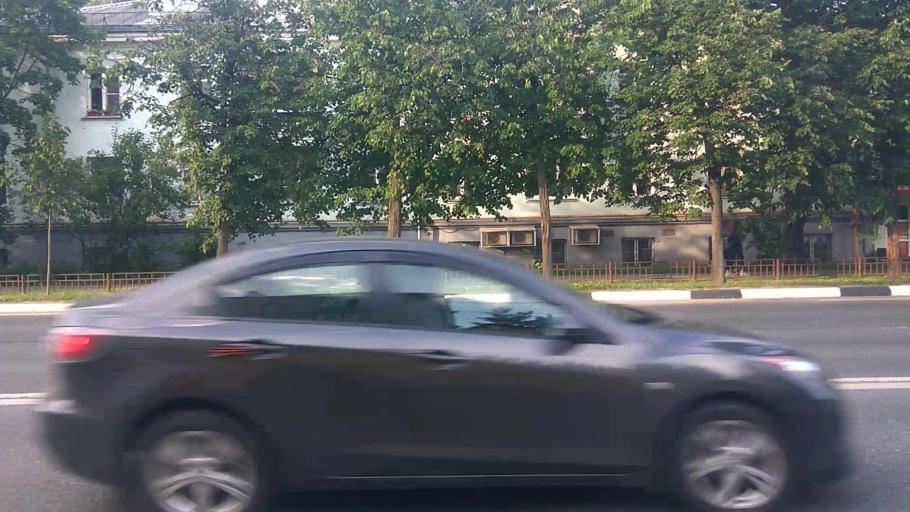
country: RU
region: Moskovskaya
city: Mytishchi
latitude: 55.9131
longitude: 37.7316
